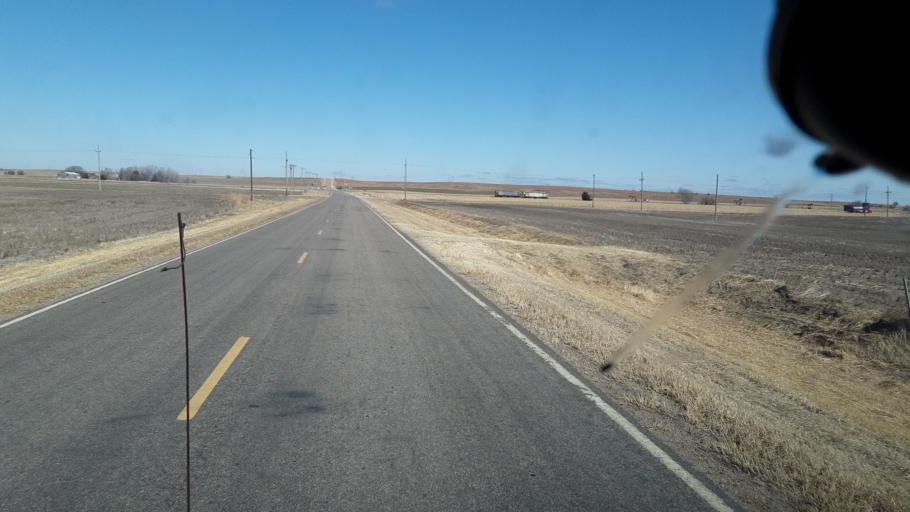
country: US
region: Kansas
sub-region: Barton County
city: Ellinwood
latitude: 38.3600
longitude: -98.6640
